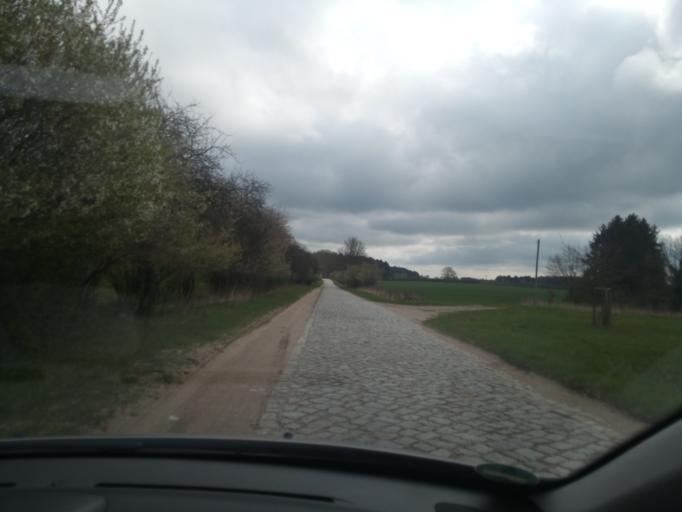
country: DE
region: Brandenburg
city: Lychen
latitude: 53.2681
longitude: 13.3606
